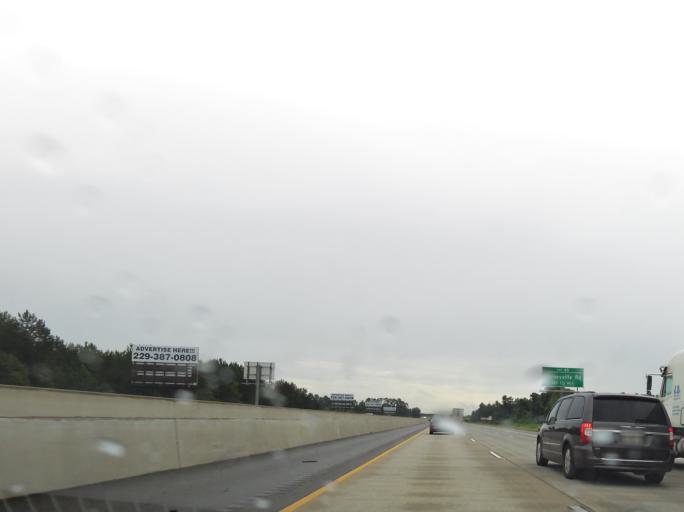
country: US
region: Georgia
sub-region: Cook County
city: Sparks
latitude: 31.2267
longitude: -83.4625
